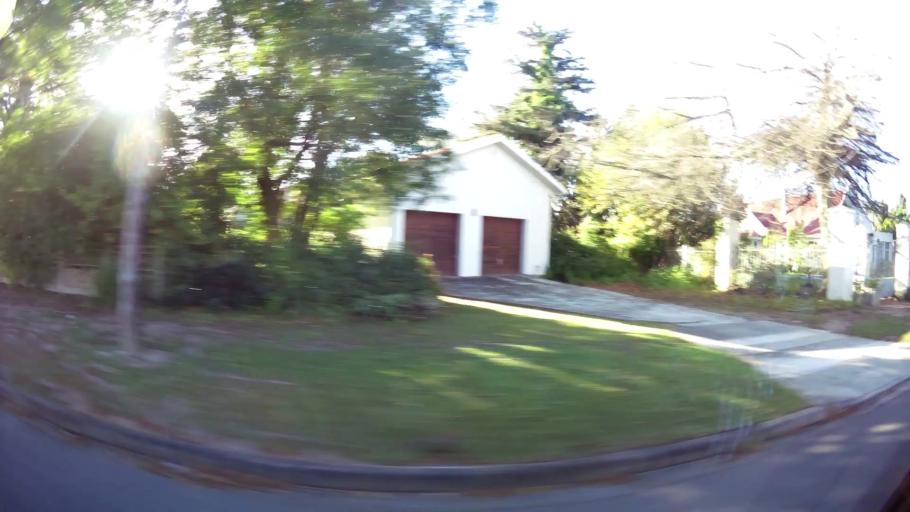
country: ZA
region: Western Cape
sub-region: Eden District Municipality
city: George
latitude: -33.9497
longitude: 22.4512
